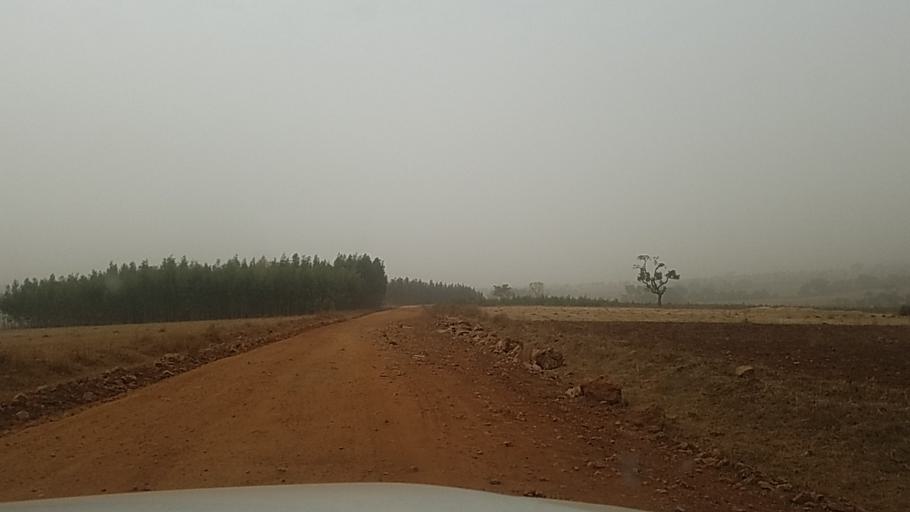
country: ET
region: Amhara
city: Bure
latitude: 10.8621
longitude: 36.4014
